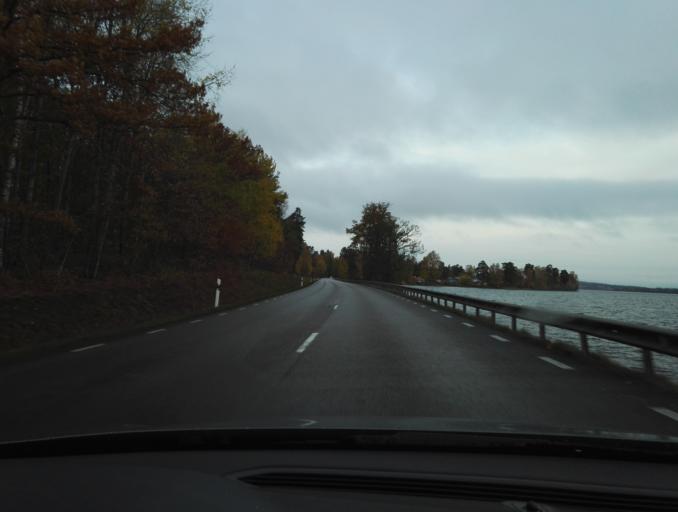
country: SE
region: Kronoberg
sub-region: Vaxjo Kommun
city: Vaexjoe
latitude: 56.9538
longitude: 14.7180
